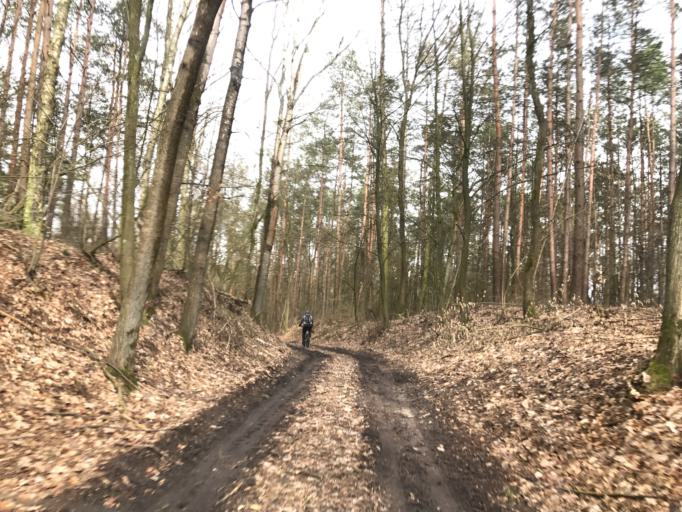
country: PL
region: Kujawsko-Pomorskie
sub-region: Powiat brodnicki
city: Gorzno
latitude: 53.2159
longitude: 19.6491
